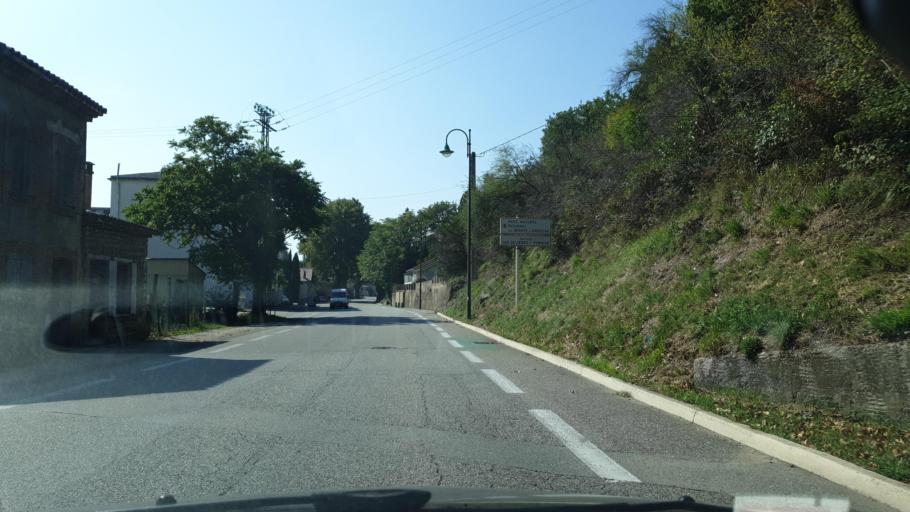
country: FR
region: Rhone-Alpes
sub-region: Departement de l'Ardeche
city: Beauchastel
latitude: 44.8300
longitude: 4.8065
